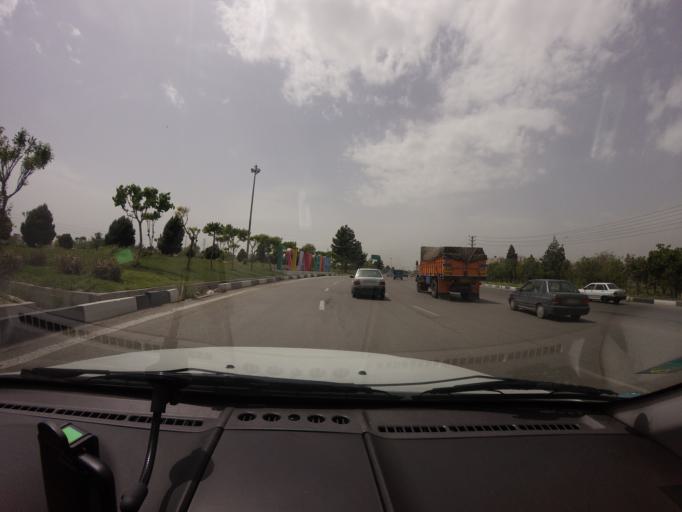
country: IR
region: Tehran
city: Eslamshahr
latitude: 35.5169
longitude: 51.2307
